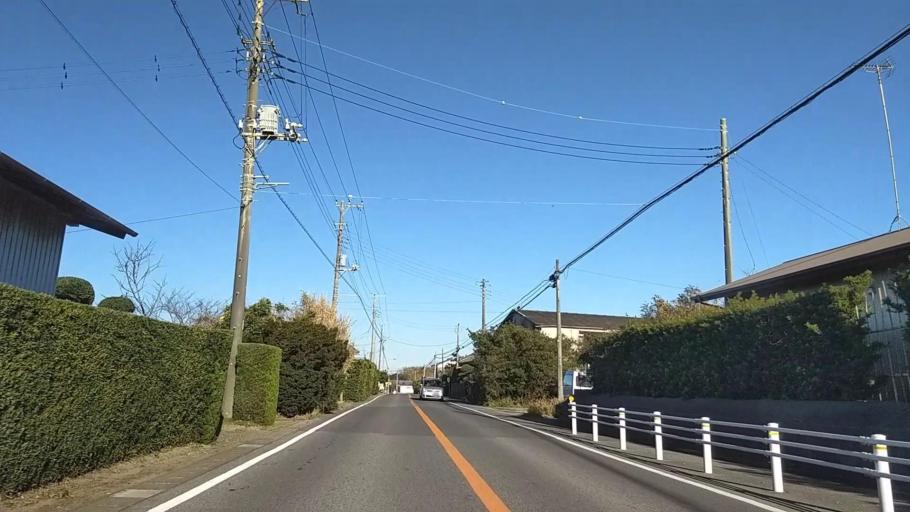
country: JP
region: Chiba
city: Yokaichiba
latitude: 35.6240
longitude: 140.5472
